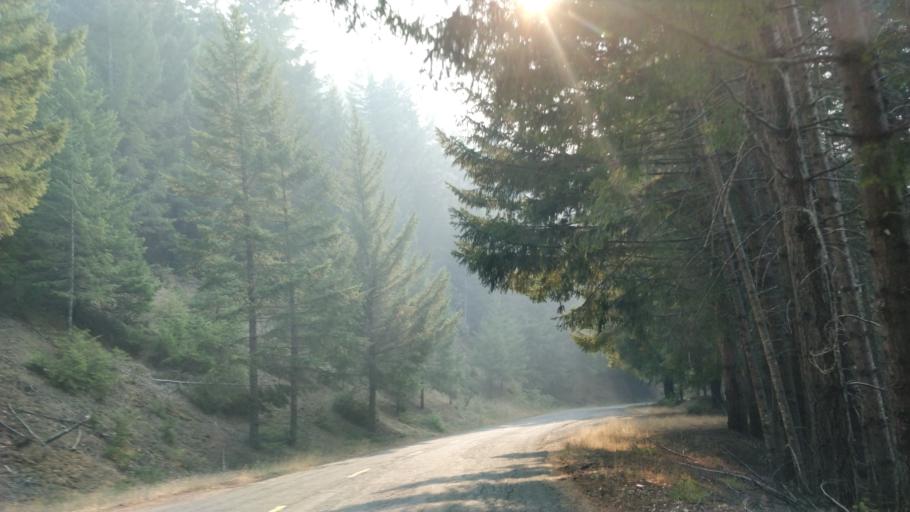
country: US
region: California
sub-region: Humboldt County
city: Rio Dell
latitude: 40.3024
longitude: -124.0572
